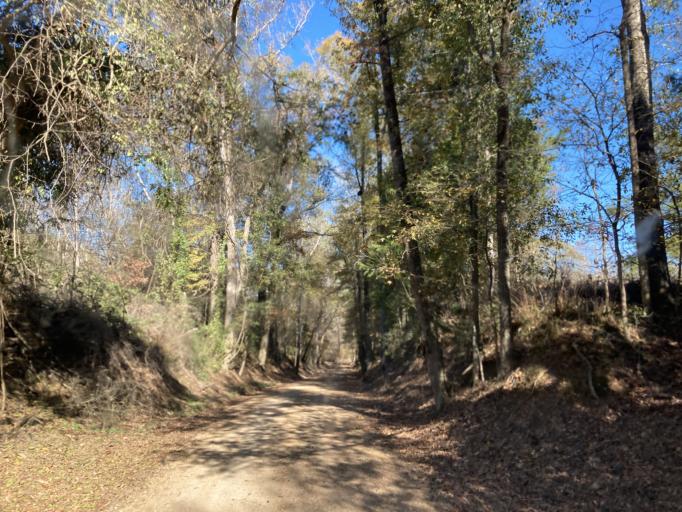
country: US
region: Mississippi
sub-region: Hinds County
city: Lynchburg
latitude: 32.5539
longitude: -90.4999
